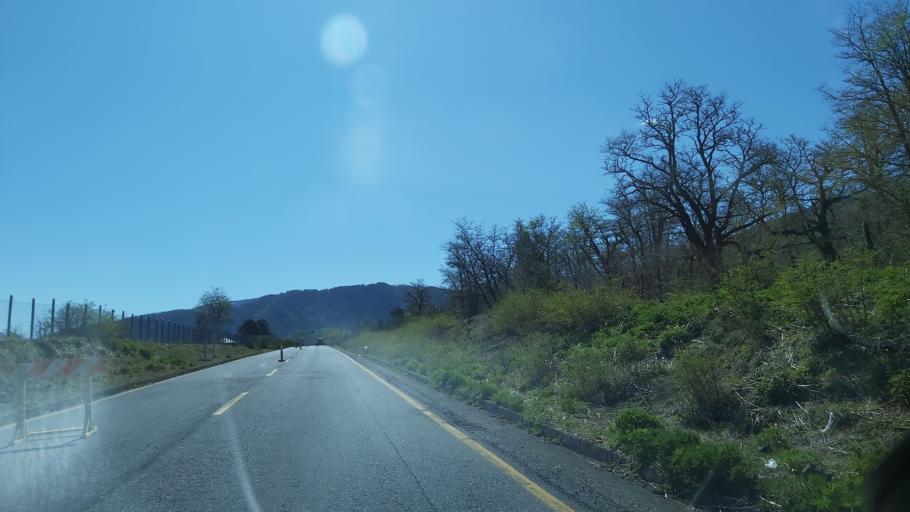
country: CL
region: Araucania
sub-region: Provincia de Cautin
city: Vilcun
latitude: -38.4670
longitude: -71.6009
